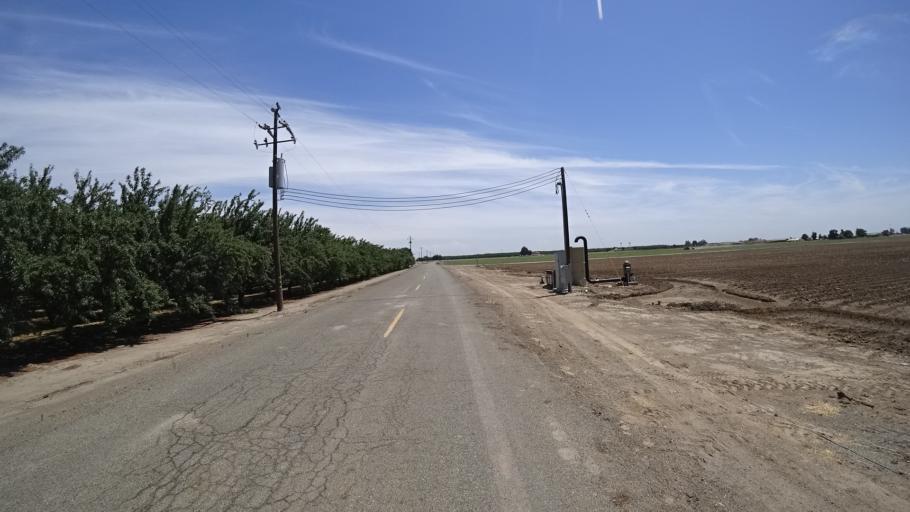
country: US
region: California
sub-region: Kings County
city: Lemoore
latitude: 36.3563
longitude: -119.7916
